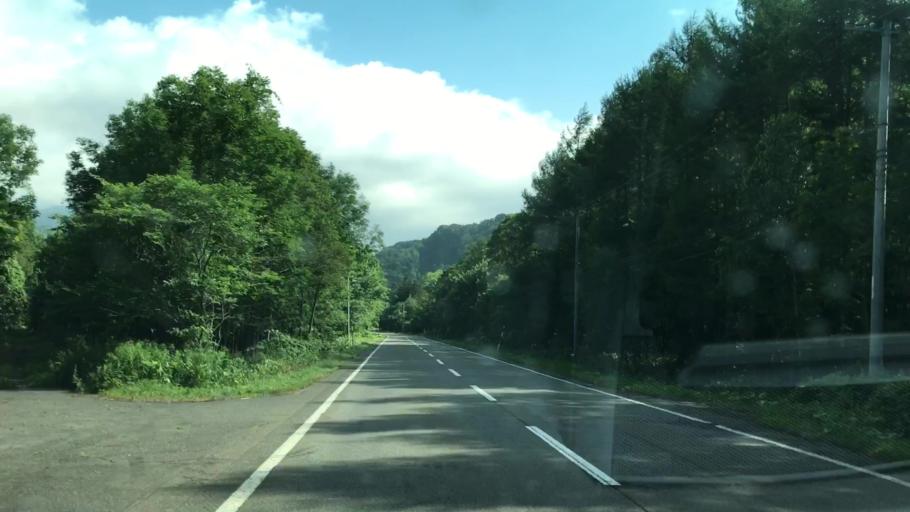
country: JP
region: Hokkaido
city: Shizunai-furukawacho
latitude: 42.8283
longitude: 142.4162
